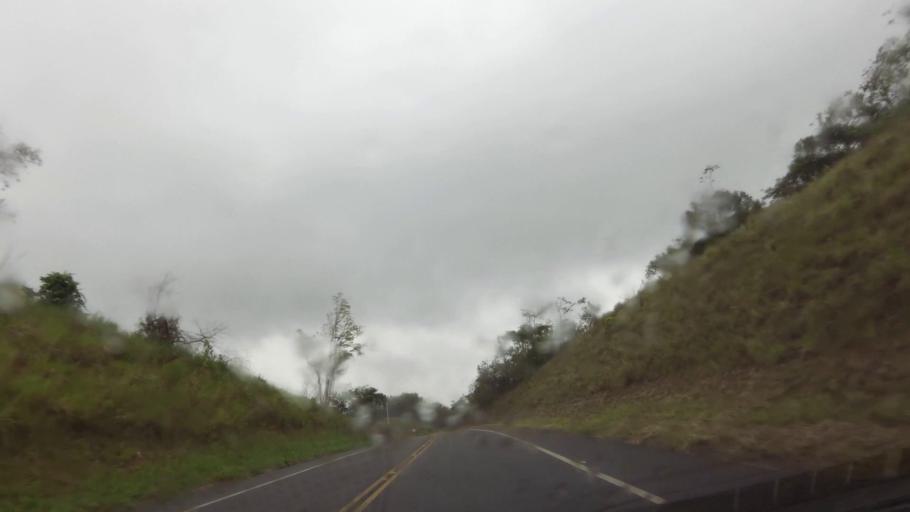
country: BR
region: Espirito Santo
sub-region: Guarapari
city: Guarapari
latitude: -20.6415
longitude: -40.5332
